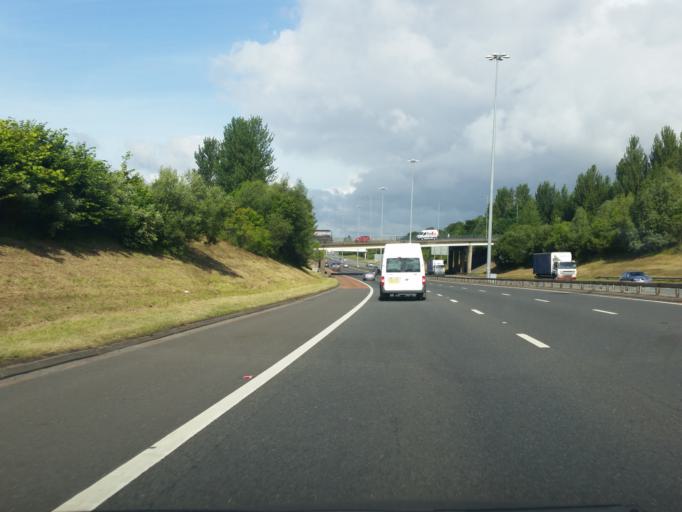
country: GB
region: Scotland
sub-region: North Lanarkshire
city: Chryston
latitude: 55.8610
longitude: -4.1051
